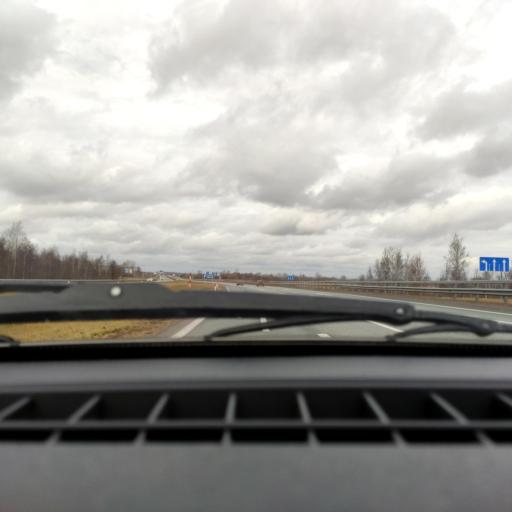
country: RU
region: Bashkortostan
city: Asanovo
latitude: 54.9653
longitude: 55.5829
